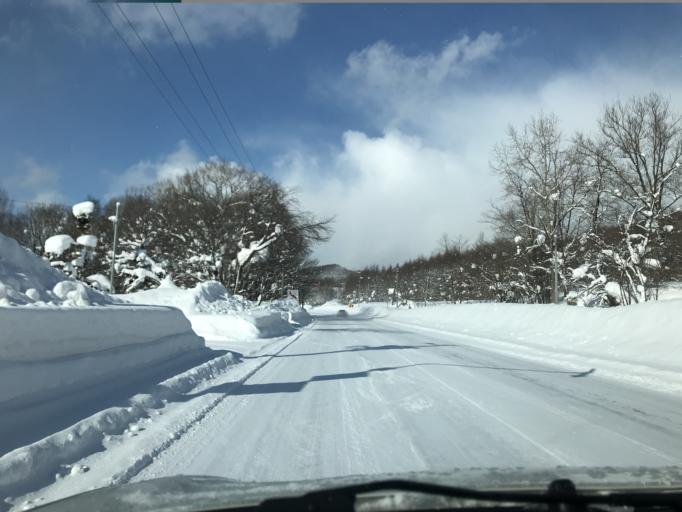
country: JP
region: Hokkaido
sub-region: Asahikawa-shi
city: Asahikawa
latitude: 43.9315
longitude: 142.4719
